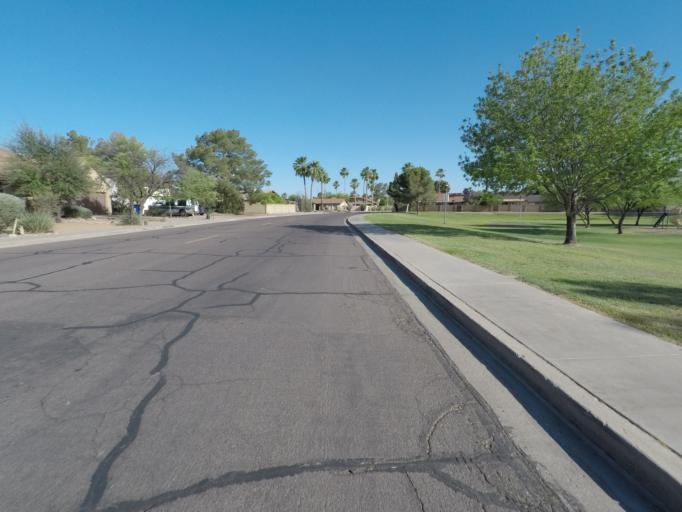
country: US
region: Arizona
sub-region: Maricopa County
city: Guadalupe
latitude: 33.3518
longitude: -111.9203
